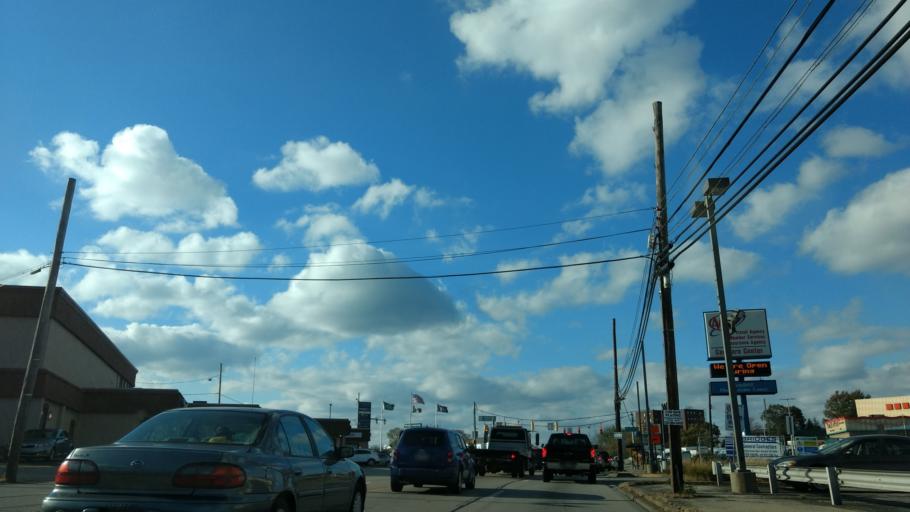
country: US
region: Pennsylvania
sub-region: Allegheny County
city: Pleasant Hills
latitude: 40.3401
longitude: -79.9635
